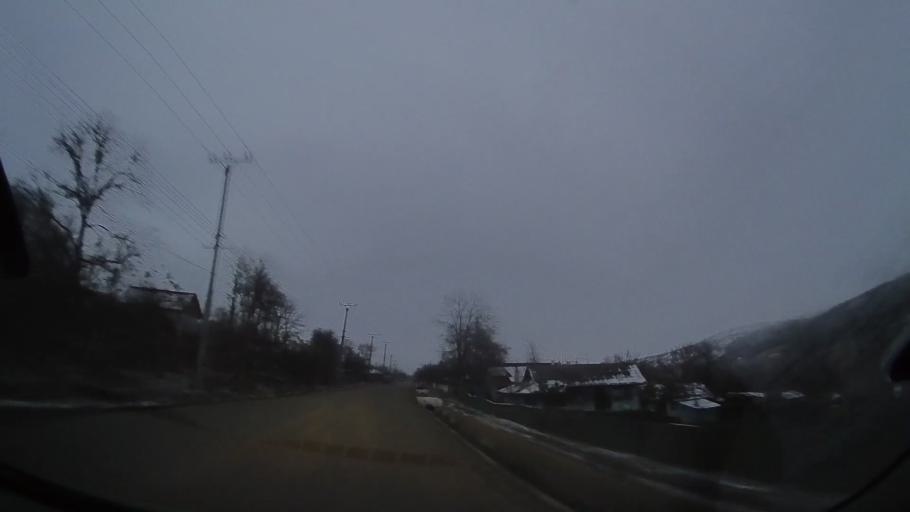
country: RO
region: Vaslui
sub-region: Comuna Vutcani
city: Vutcani
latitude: 46.4112
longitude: 27.9947
